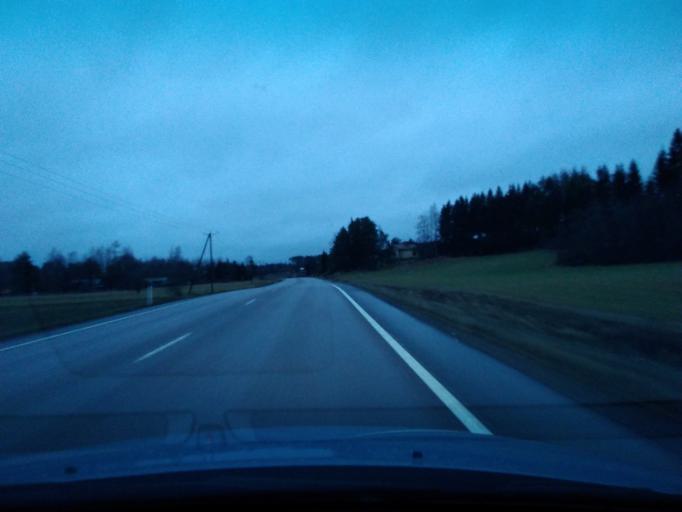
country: FI
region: Uusimaa
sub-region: Porvoo
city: Askola
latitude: 60.4578
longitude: 25.5807
